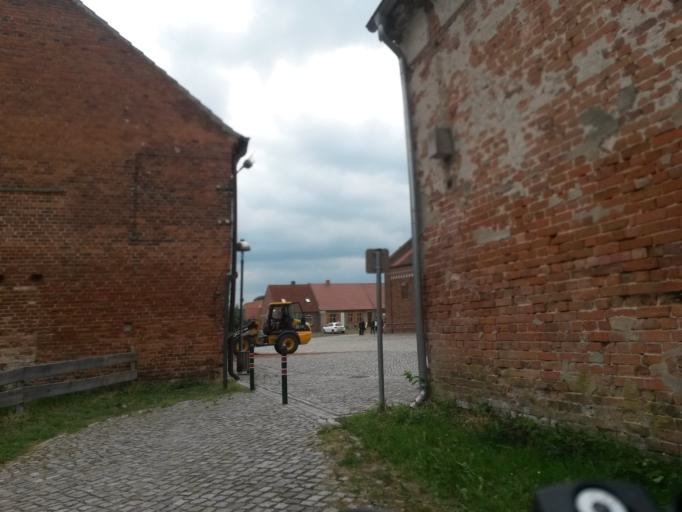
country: DE
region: Saxony-Anhalt
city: Jerichow
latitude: 52.5029
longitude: 12.0158
